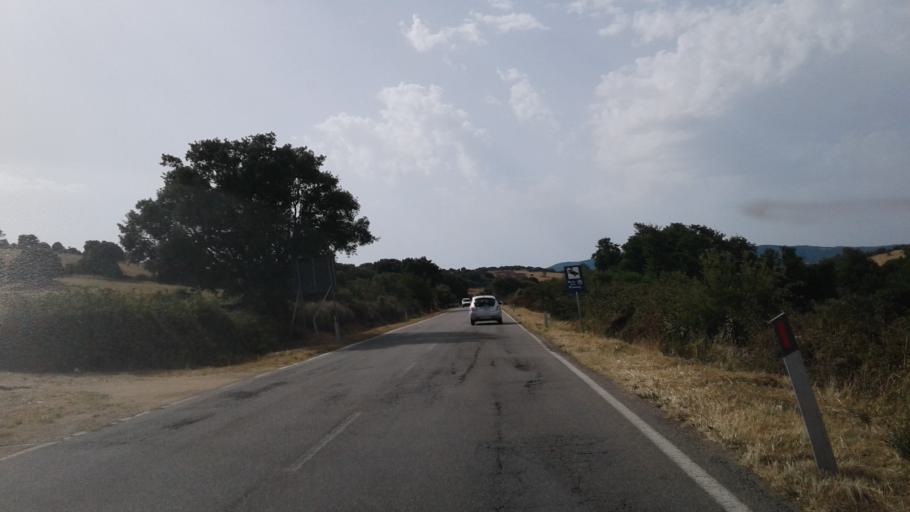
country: IT
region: Sardinia
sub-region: Provincia di Olbia-Tempio
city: Sant'Antonio di Gallura
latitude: 40.9692
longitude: 9.2742
